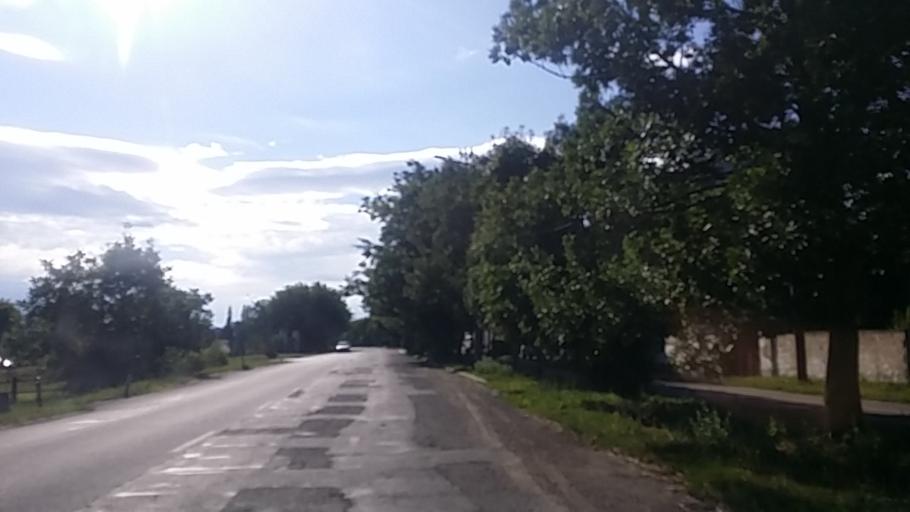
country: HU
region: Pest
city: Vac
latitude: 47.7744
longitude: 19.1472
